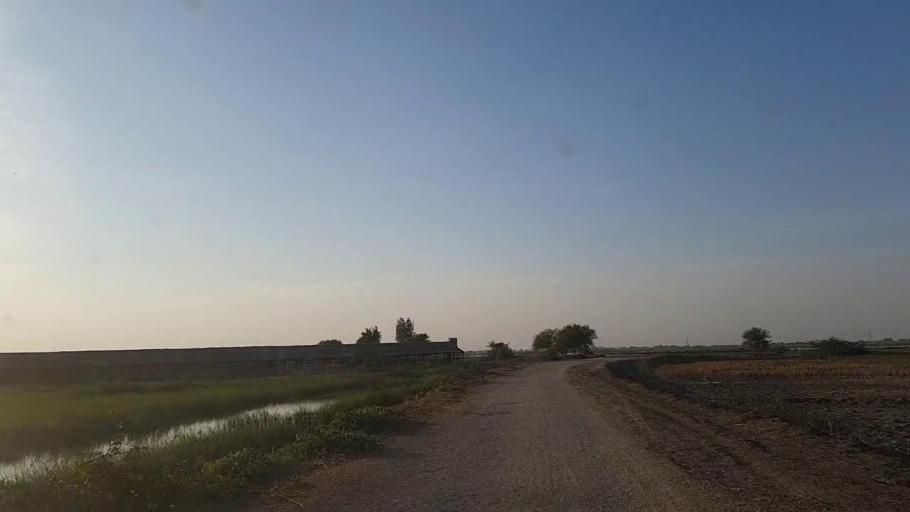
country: PK
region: Sindh
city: Mirpur Batoro
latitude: 24.6842
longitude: 68.2095
